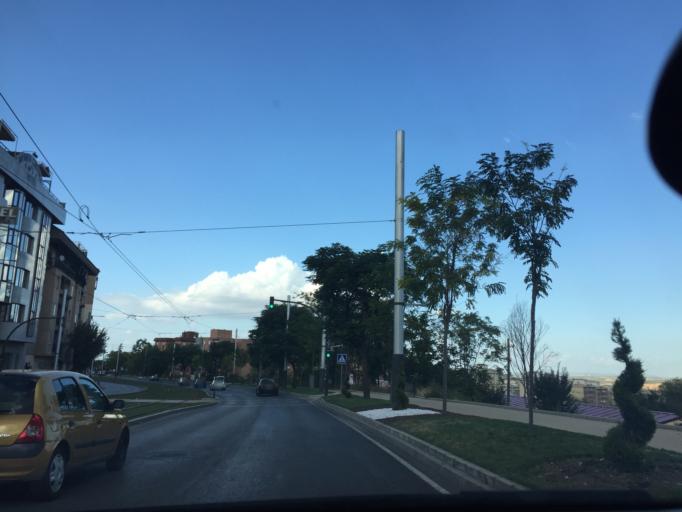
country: ES
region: Andalusia
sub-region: Provincia de Jaen
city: Jaen
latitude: 37.7808
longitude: -3.7838
